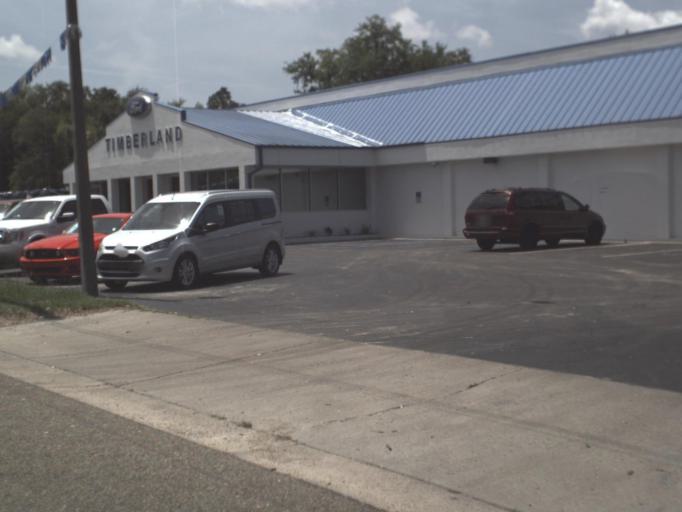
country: US
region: Florida
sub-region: Taylor County
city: Perry
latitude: 30.0901
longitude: -83.5750
